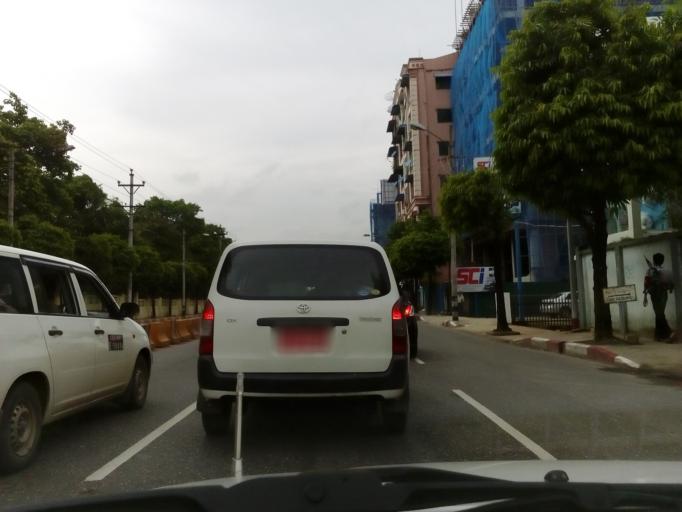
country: MM
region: Yangon
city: Yangon
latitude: 16.8598
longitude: 96.1559
